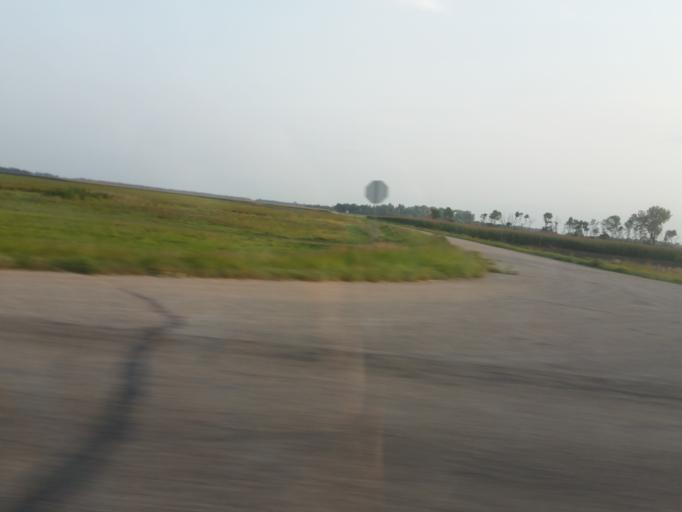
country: US
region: North Dakota
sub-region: Grand Forks County
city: Larimore
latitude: 47.7443
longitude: -97.6022
